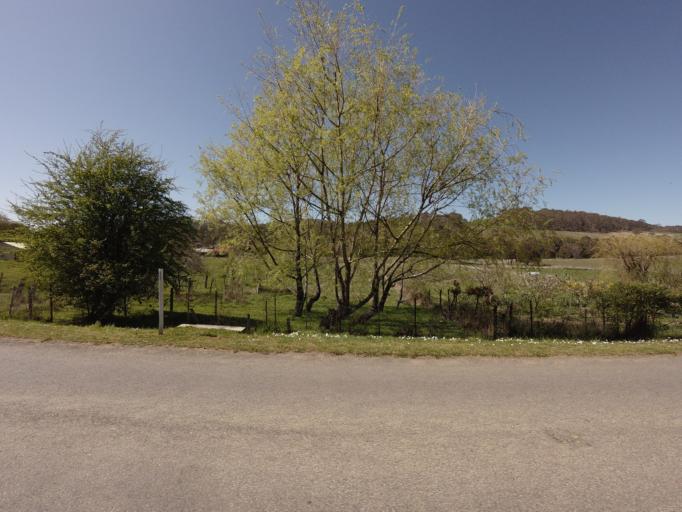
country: AU
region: Tasmania
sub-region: Derwent Valley
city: New Norfolk
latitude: -42.6194
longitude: 146.7171
